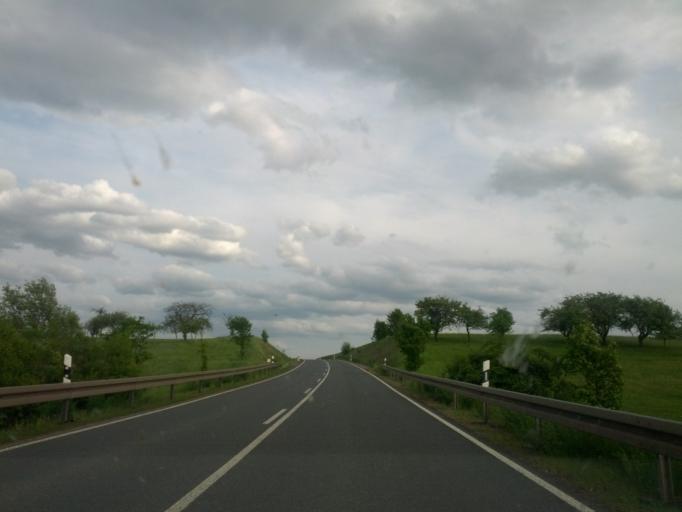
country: DE
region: Thuringia
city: Horselgau
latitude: 50.9016
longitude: 10.6136
